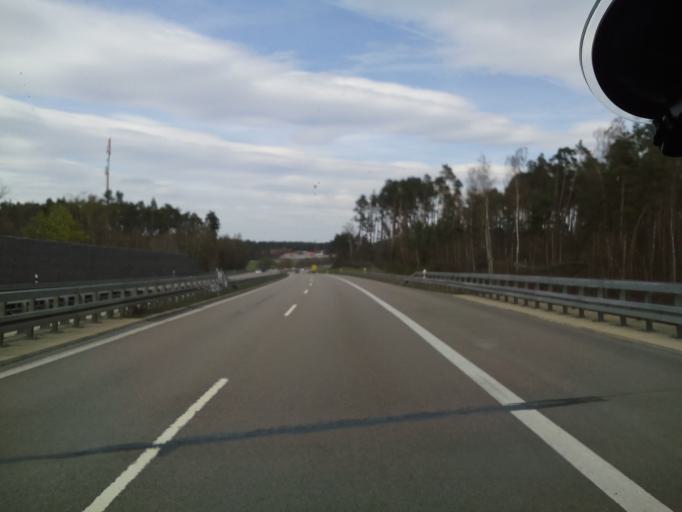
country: DE
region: Bavaria
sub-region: Regierungsbezirk Mittelfranken
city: Roth
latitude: 49.2246
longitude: 11.0898
